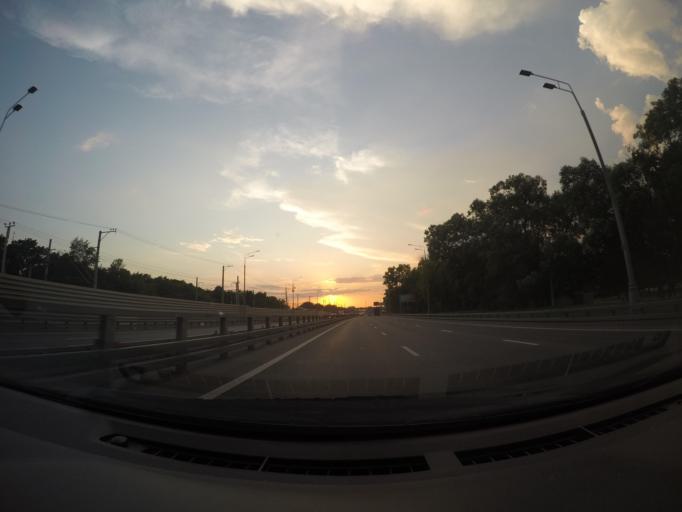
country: RU
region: Moscow
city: Perovo
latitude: 55.7218
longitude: 37.8019
